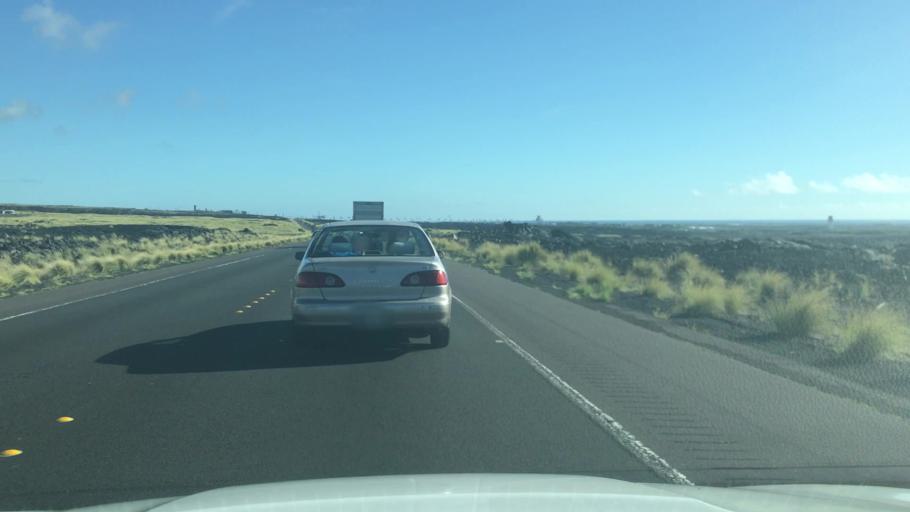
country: US
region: Hawaii
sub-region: Hawaii County
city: Kalaoa
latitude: 19.7596
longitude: -156.0255
